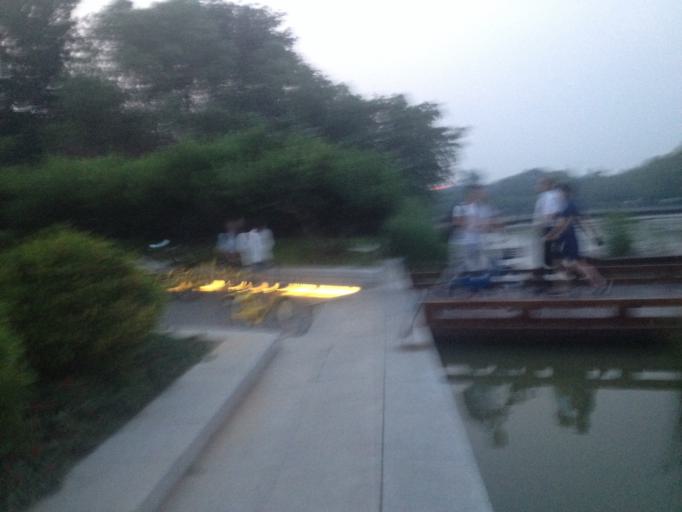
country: CN
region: Beijing
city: Datun
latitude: 40.0082
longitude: 116.3911
